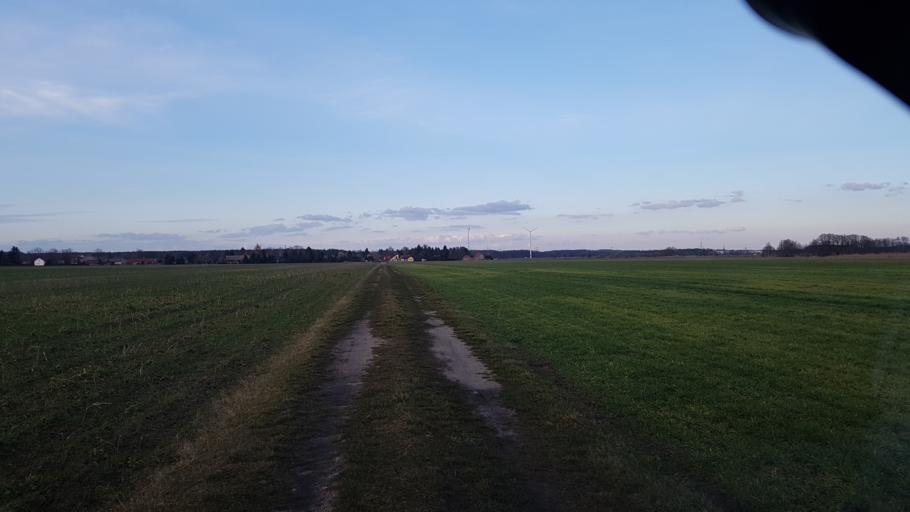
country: DE
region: Brandenburg
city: Schonborn
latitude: 51.5865
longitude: 13.5014
